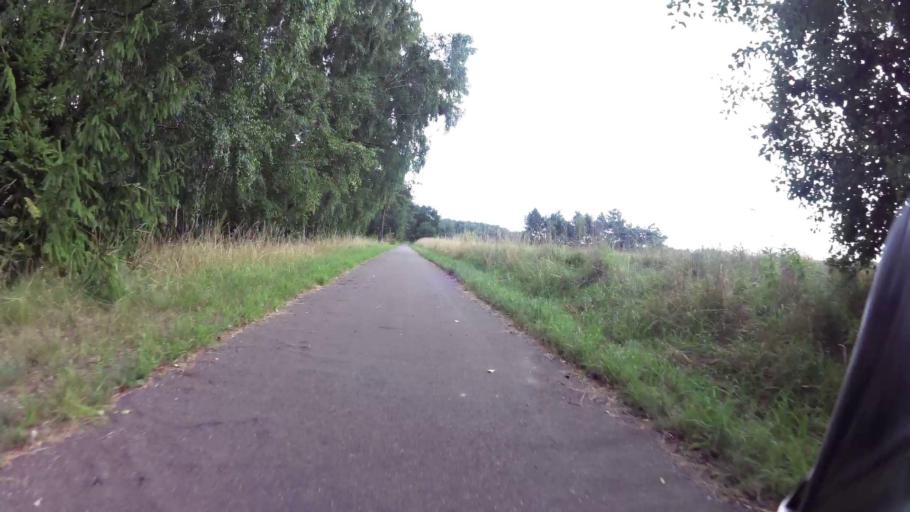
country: PL
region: West Pomeranian Voivodeship
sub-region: Powiat gryfinski
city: Banie
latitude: 53.0496
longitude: 14.6310
